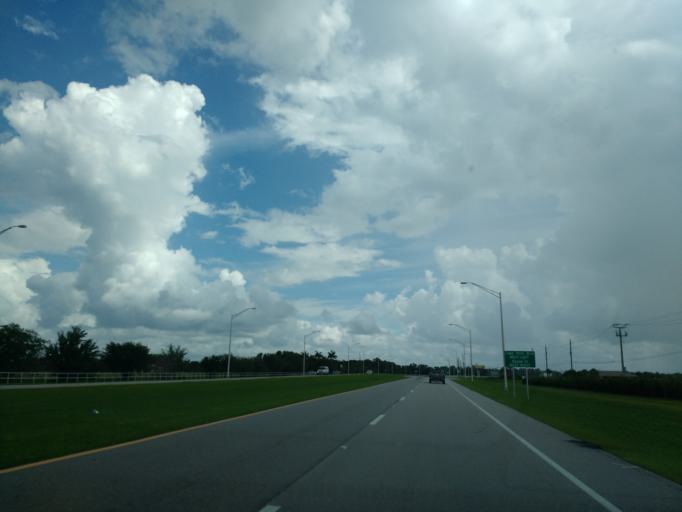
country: US
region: Florida
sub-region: Lee County
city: Burnt Store Marina
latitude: 26.7924
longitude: -82.0379
